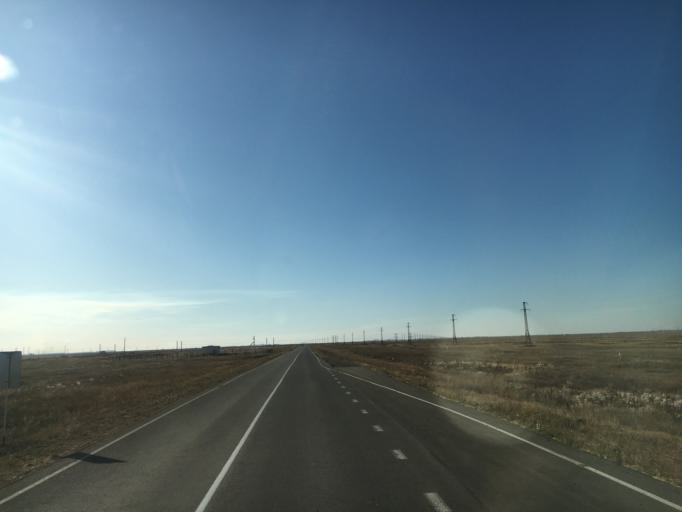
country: KZ
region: Qaraghandy
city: Tokarevka
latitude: 50.0995
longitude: 73.3077
